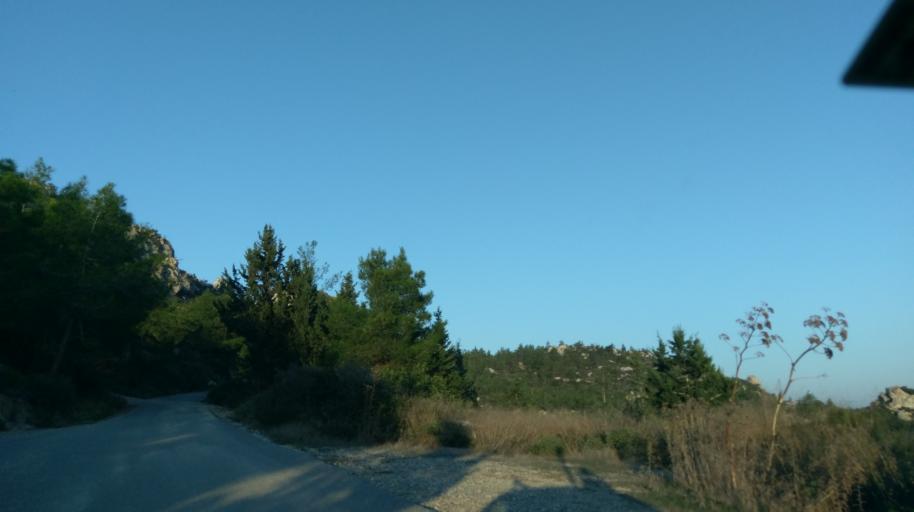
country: CY
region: Ammochostos
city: Trikomo
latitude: 35.4024
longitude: 33.9183
